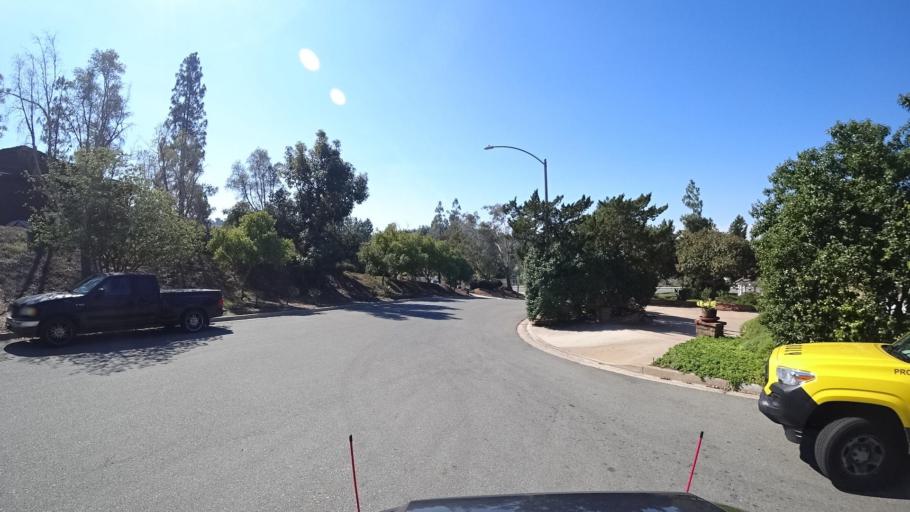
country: US
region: California
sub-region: San Diego County
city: Granite Hills
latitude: 32.7845
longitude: -116.8999
